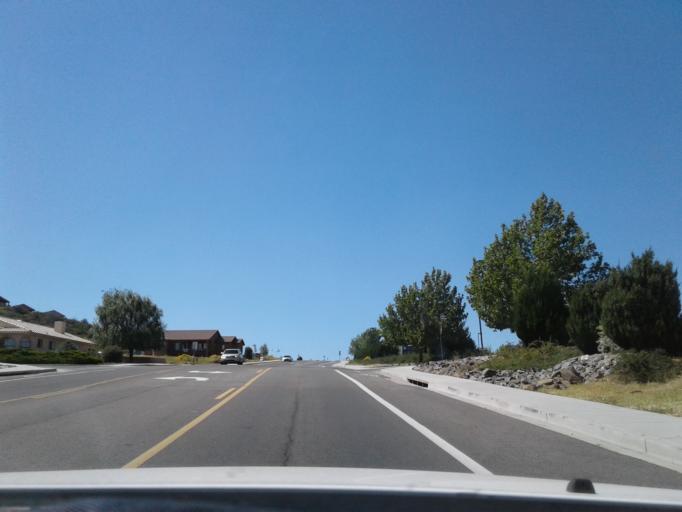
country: US
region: Arizona
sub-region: Yavapai County
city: Prescott
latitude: 34.5737
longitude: -112.4444
